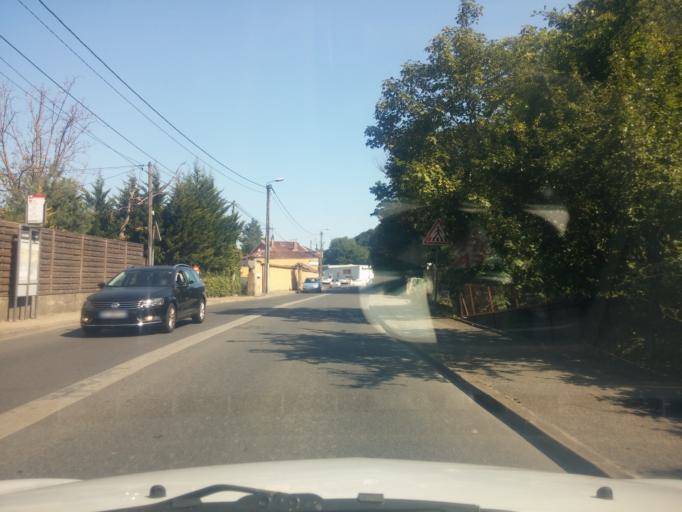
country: FR
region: Rhone-Alpes
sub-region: Departement du Rhone
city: Oullins
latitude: 45.7222
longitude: 4.7866
